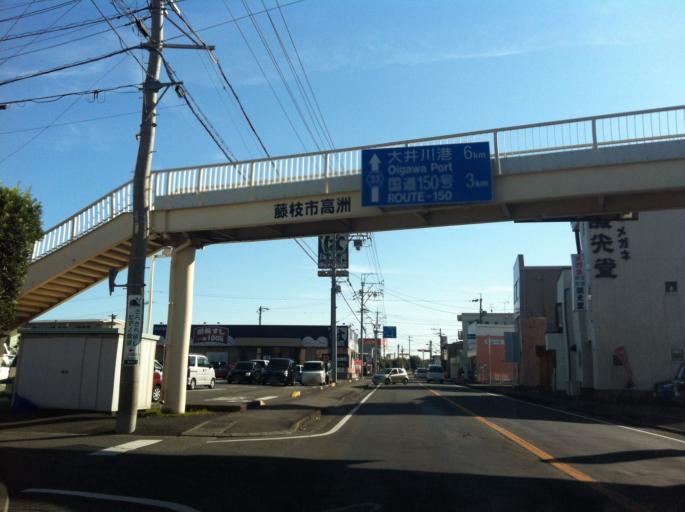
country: JP
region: Shizuoka
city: Fujieda
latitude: 34.8414
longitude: 138.2628
